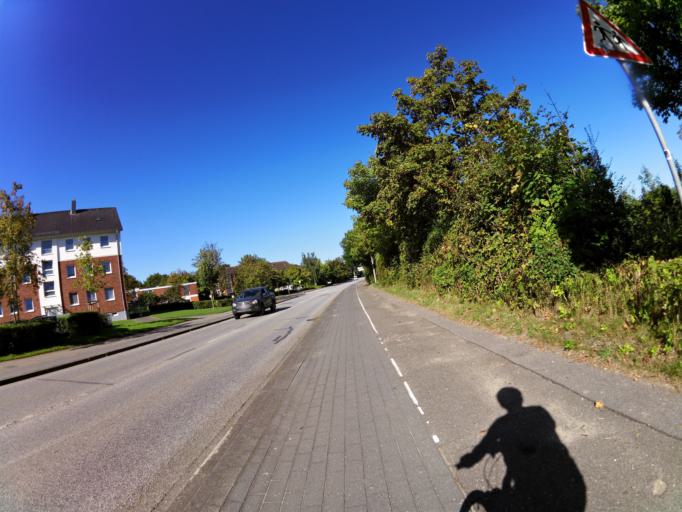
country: DE
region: Schleswig-Holstein
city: Eckernforde
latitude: 54.4568
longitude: 9.8310
